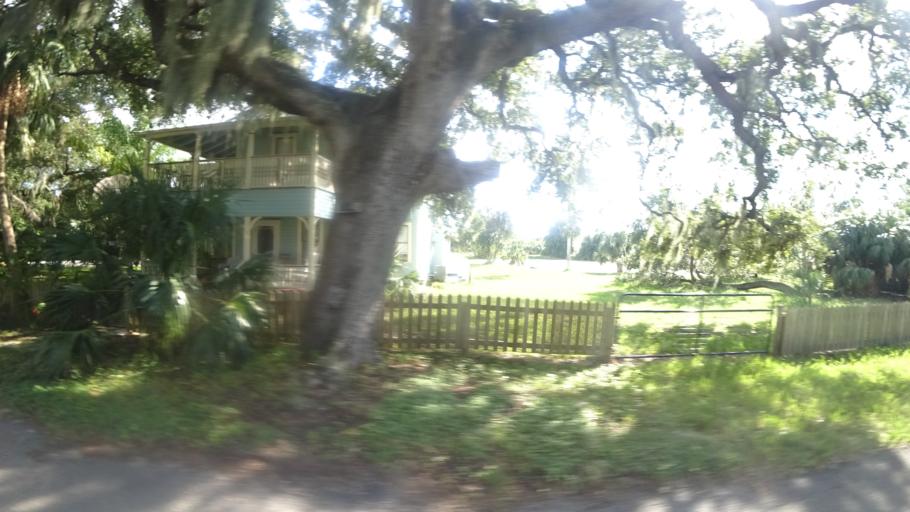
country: US
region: Florida
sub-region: Manatee County
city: Memphis
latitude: 27.5685
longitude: -82.5895
